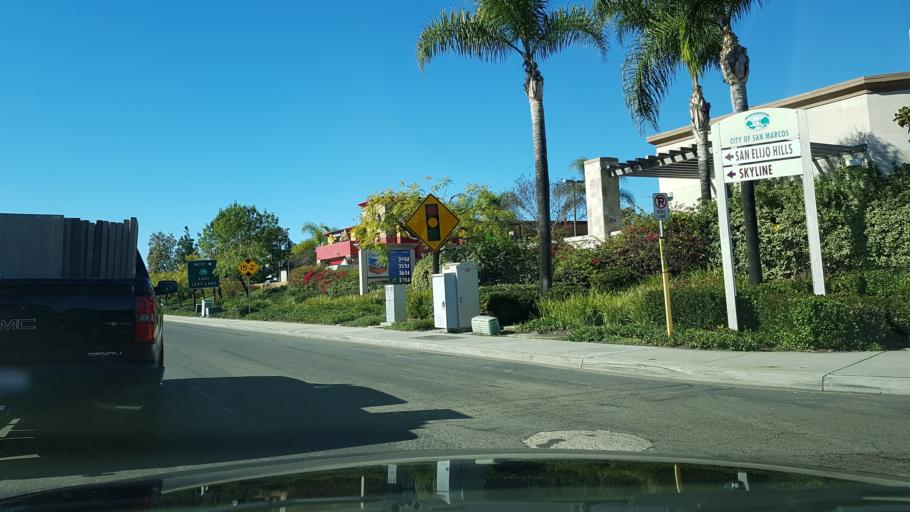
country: US
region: California
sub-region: San Diego County
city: San Marcos
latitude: 33.1386
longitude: -117.1744
